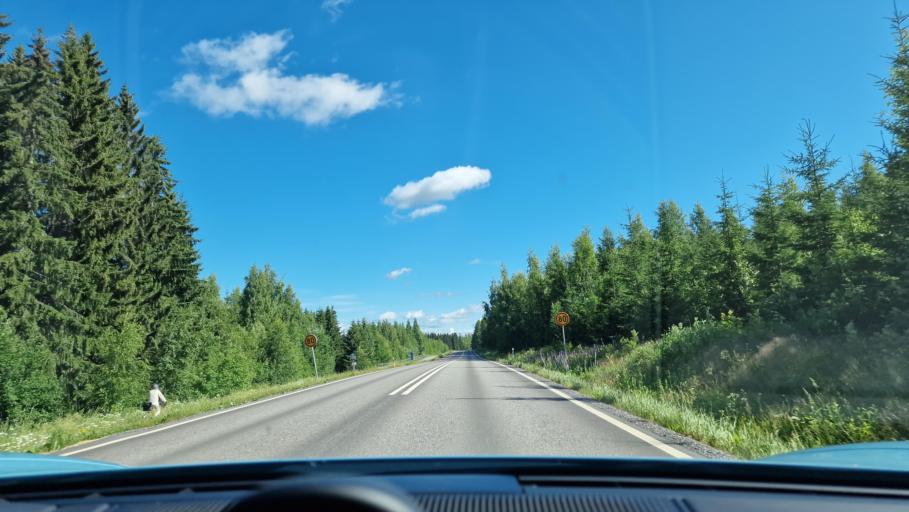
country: FI
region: Pirkanmaa
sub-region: Tampere
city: Kangasala
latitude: 61.4652
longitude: 24.1256
